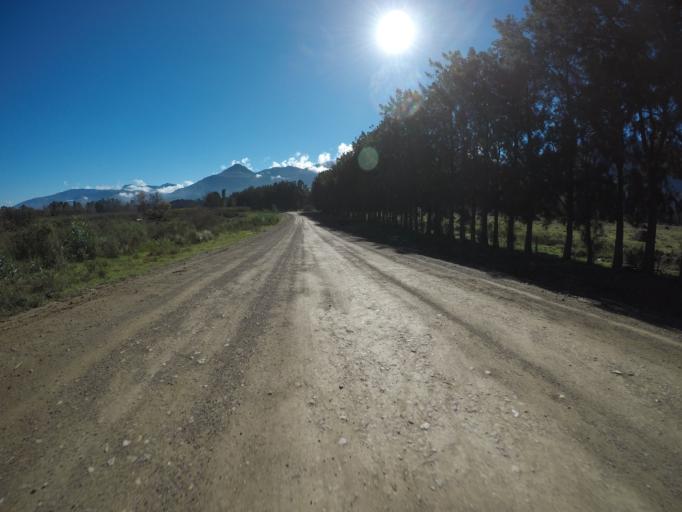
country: ZA
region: Western Cape
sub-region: Overberg District Municipality
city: Caledon
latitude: -34.0778
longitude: 19.6442
